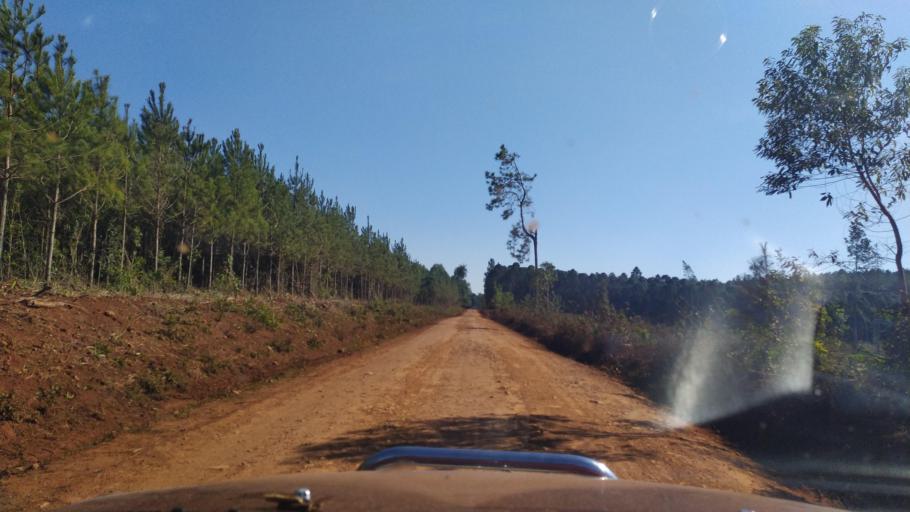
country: AR
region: Misiones
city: El Alcazar
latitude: -26.7345
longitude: -54.6660
